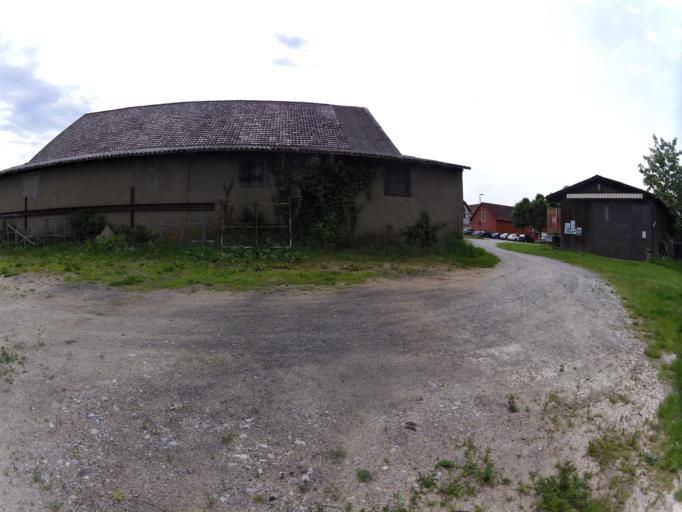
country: DE
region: Bavaria
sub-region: Regierungsbezirk Unterfranken
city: Nordheim
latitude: 49.8610
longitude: 10.1824
